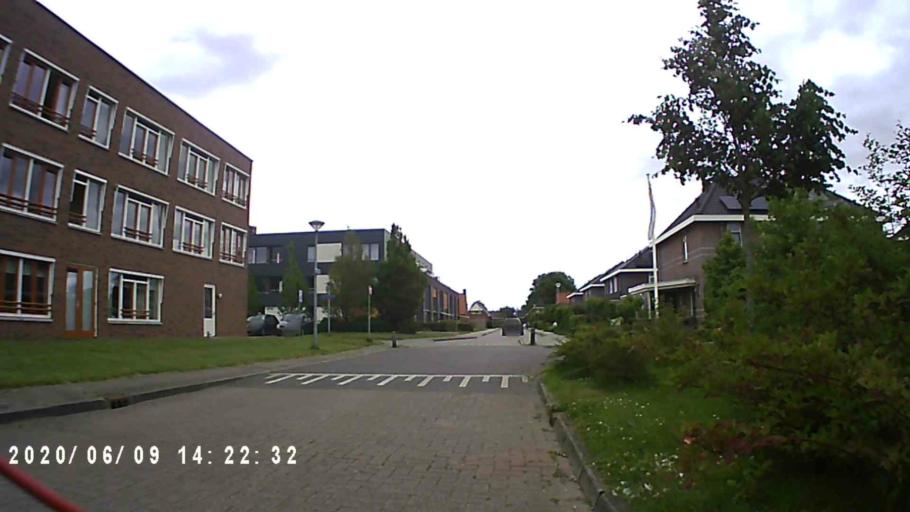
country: NL
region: Groningen
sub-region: Gemeente Bedum
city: Bedum
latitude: 53.3004
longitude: 6.5909
